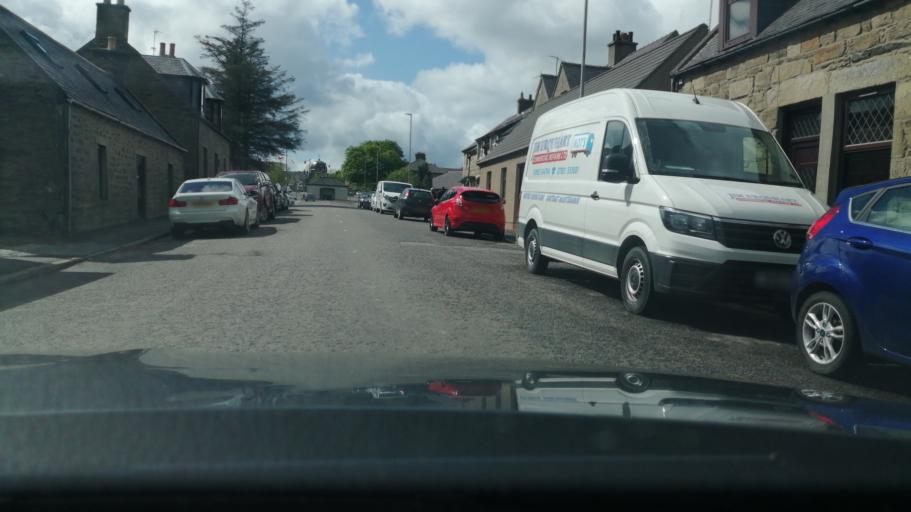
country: GB
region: Scotland
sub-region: Moray
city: Keith
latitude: 57.5381
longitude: -2.9463
